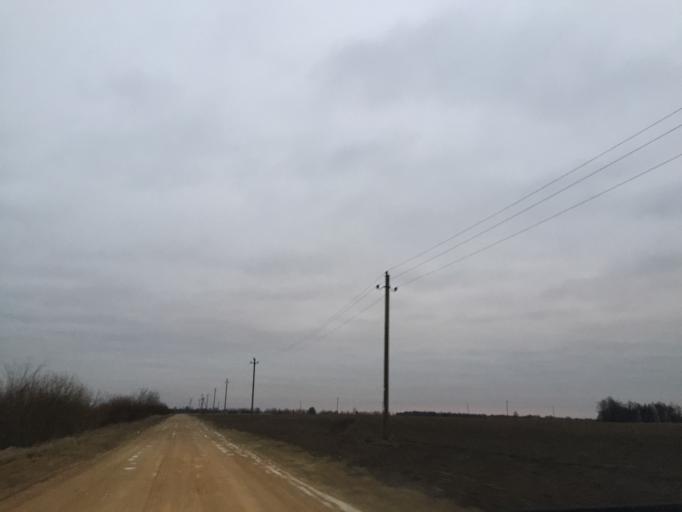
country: LT
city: Zagare
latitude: 56.3423
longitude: 23.2702
